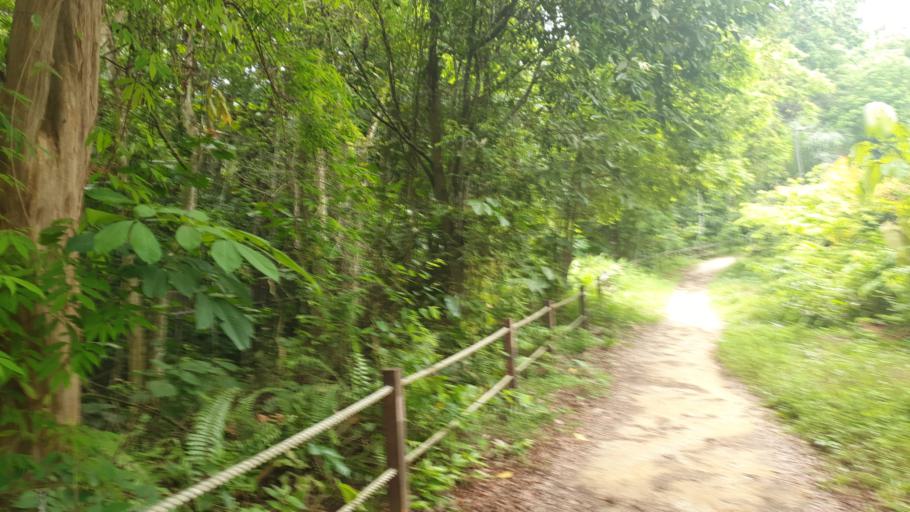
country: SG
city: Singapore
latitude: 1.3576
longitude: 103.8193
